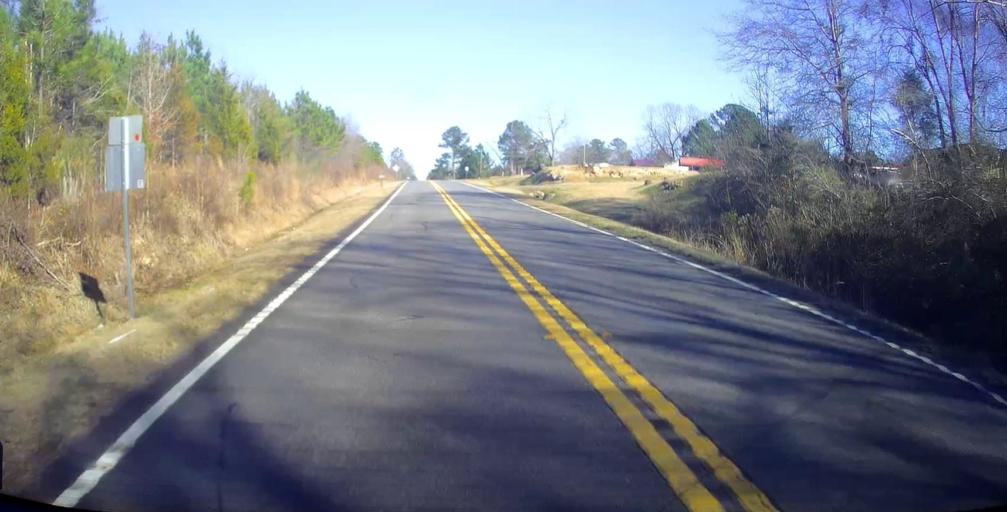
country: US
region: Georgia
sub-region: Talbot County
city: Talbotton
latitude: 32.6728
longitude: -84.5282
